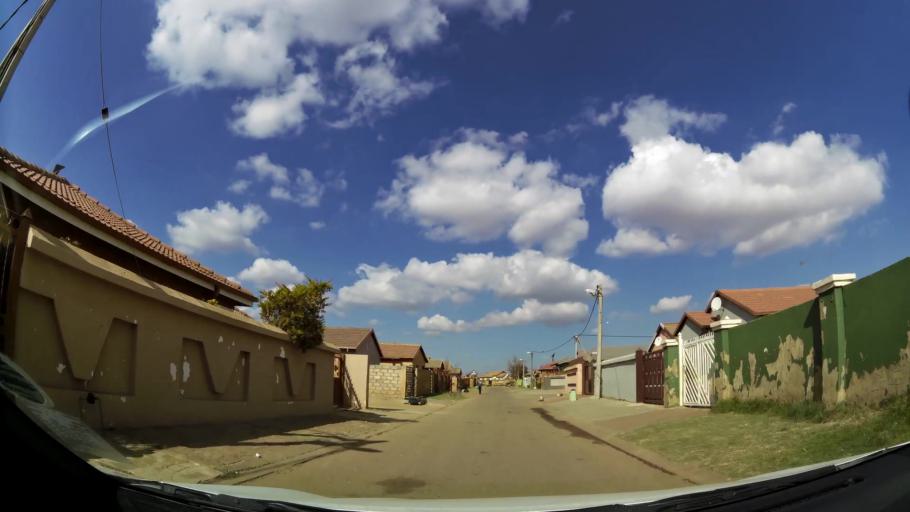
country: ZA
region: Gauteng
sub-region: City of Tshwane Metropolitan Municipality
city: Cullinan
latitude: -25.7045
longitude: 28.4160
